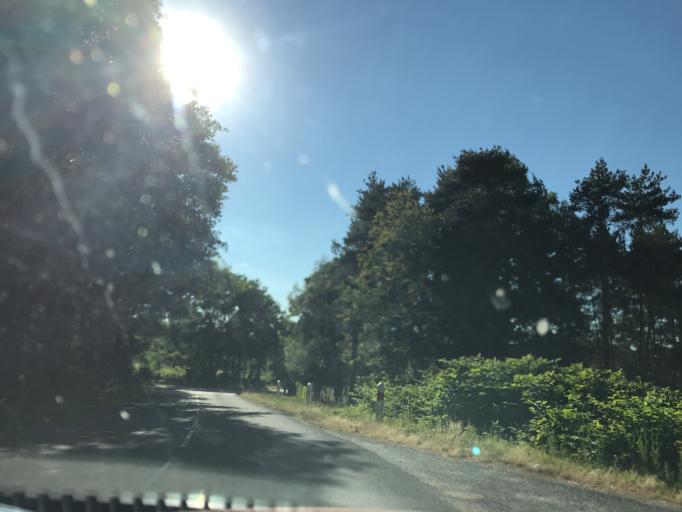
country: FR
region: Auvergne
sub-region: Departement du Puy-de-Dome
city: Peschadoires
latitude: 45.8627
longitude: 3.5088
